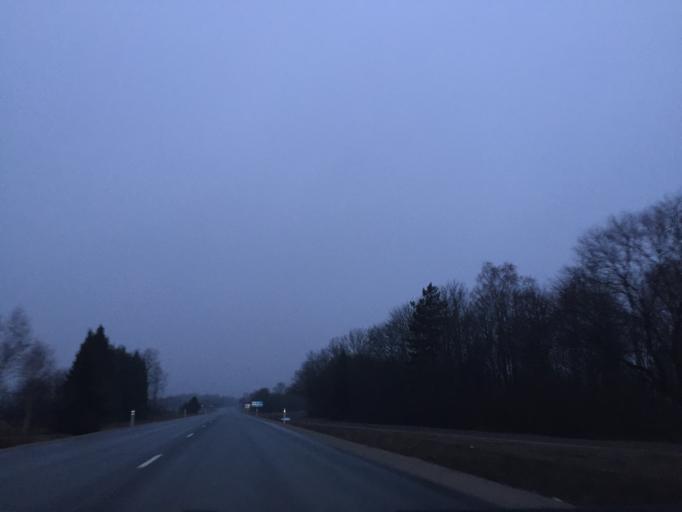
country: EE
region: Laeaene
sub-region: Lihula vald
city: Lihula
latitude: 58.6232
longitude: 23.6399
